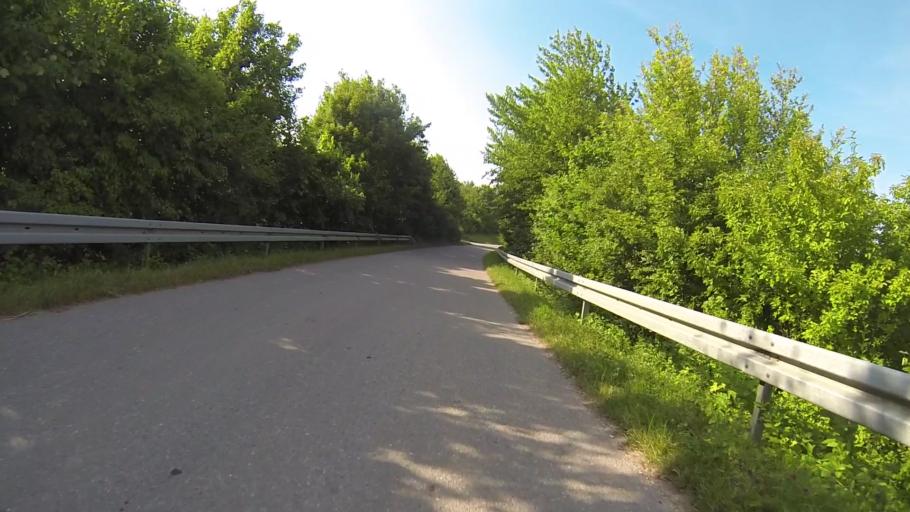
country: DE
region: Bavaria
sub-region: Swabia
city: Neu-Ulm
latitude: 48.4013
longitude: 10.0455
